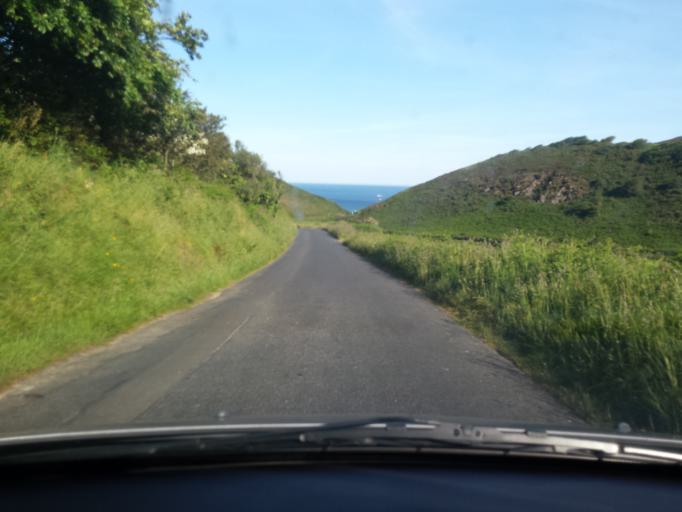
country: FR
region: Lower Normandy
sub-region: Departement de la Manche
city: Beaumont-Hague
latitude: 49.6878
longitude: -1.9281
